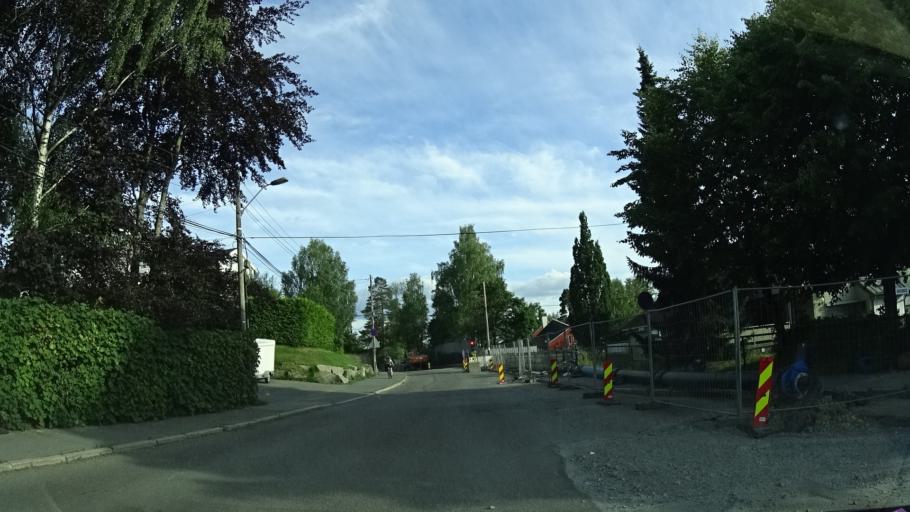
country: NO
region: Oslo
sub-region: Oslo
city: Sjolyststranda
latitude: 59.9540
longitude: 10.6580
